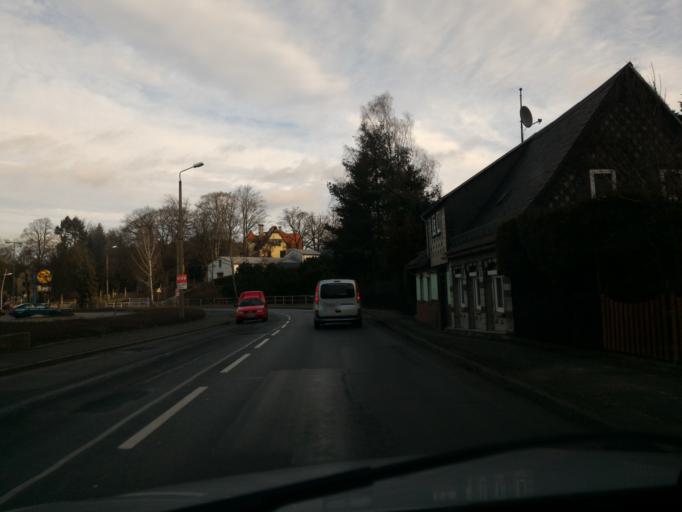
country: DE
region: Saxony
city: Ebersbach
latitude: 51.0121
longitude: 14.5818
